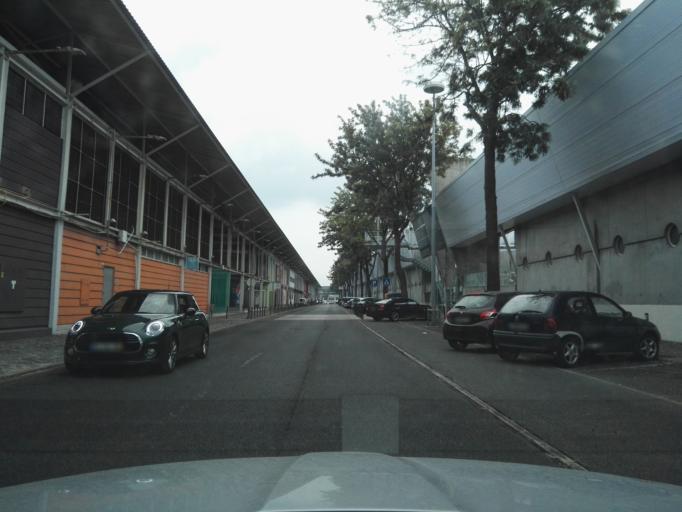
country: PT
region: Lisbon
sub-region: Loures
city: Moscavide
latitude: 38.7730
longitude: -9.0925
